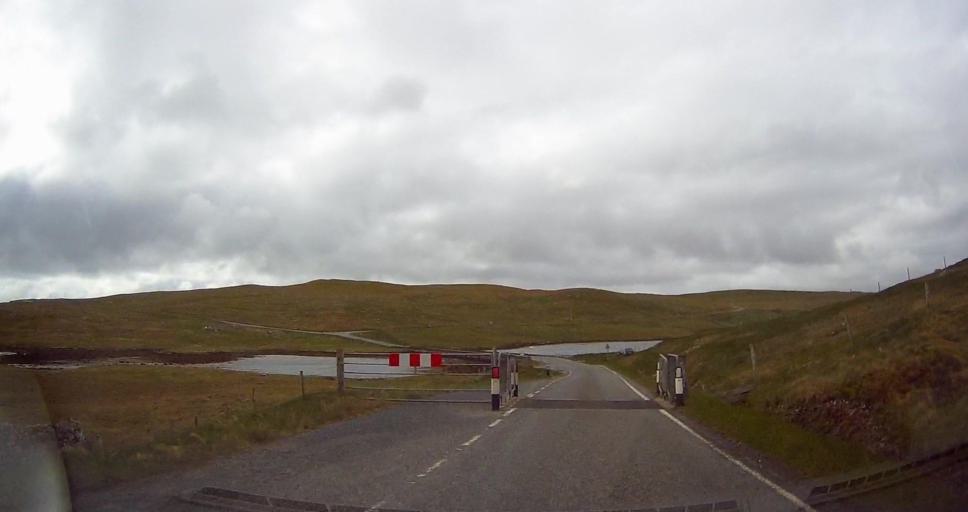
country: GB
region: Scotland
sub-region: Shetland Islands
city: Sandwick
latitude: 60.2445
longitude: -1.5266
